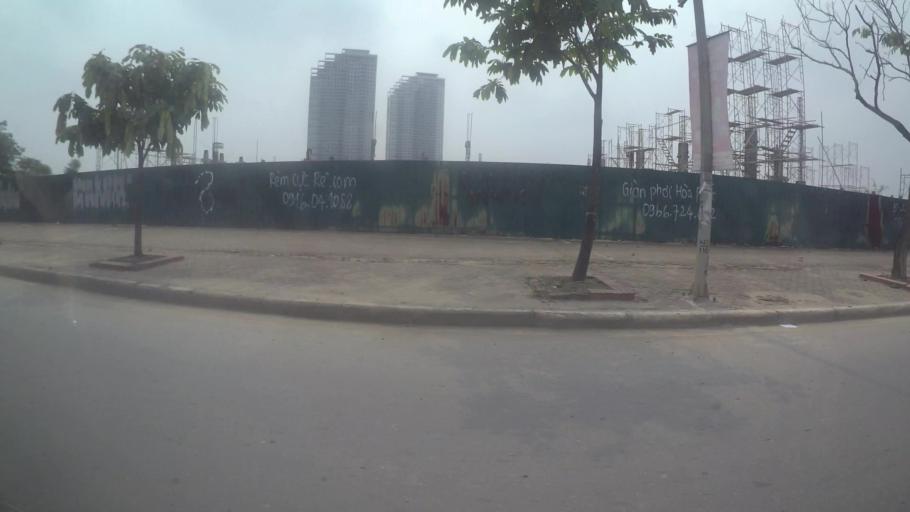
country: VN
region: Ha Noi
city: Thanh Xuan
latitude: 21.0083
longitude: 105.7734
